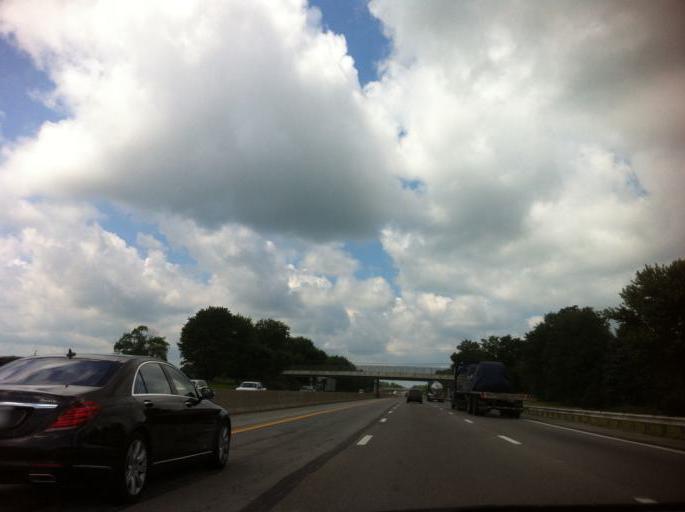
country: US
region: Ohio
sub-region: Huron County
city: Wakeman
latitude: 41.3339
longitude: -82.4060
